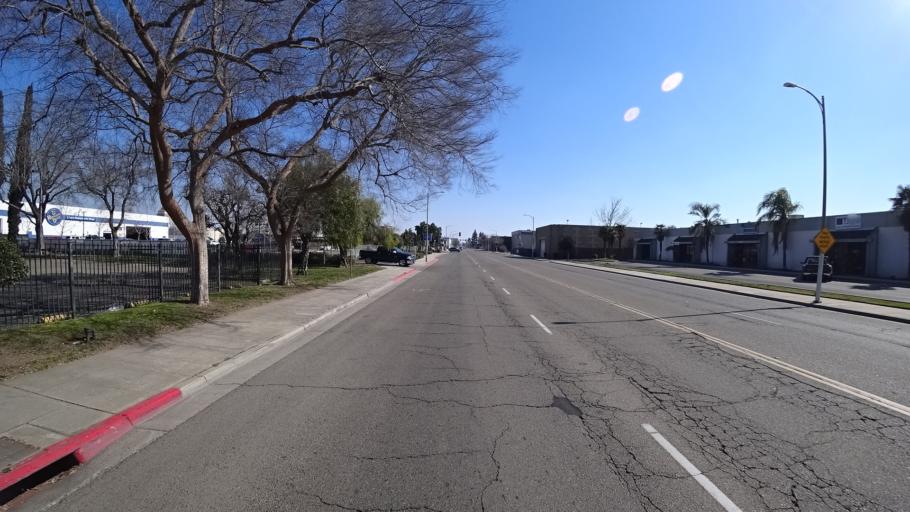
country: US
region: California
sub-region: Fresno County
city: Fresno
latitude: 36.7357
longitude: -119.8025
